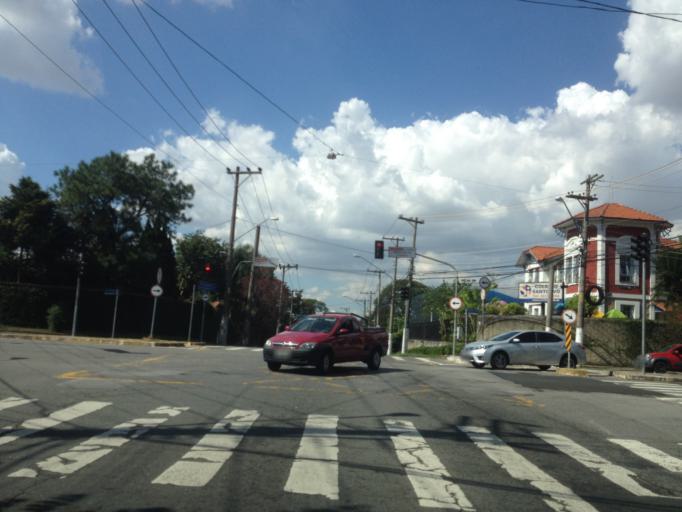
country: BR
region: Sao Paulo
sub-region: Osasco
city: Osasco
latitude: -23.5243
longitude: -46.7193
